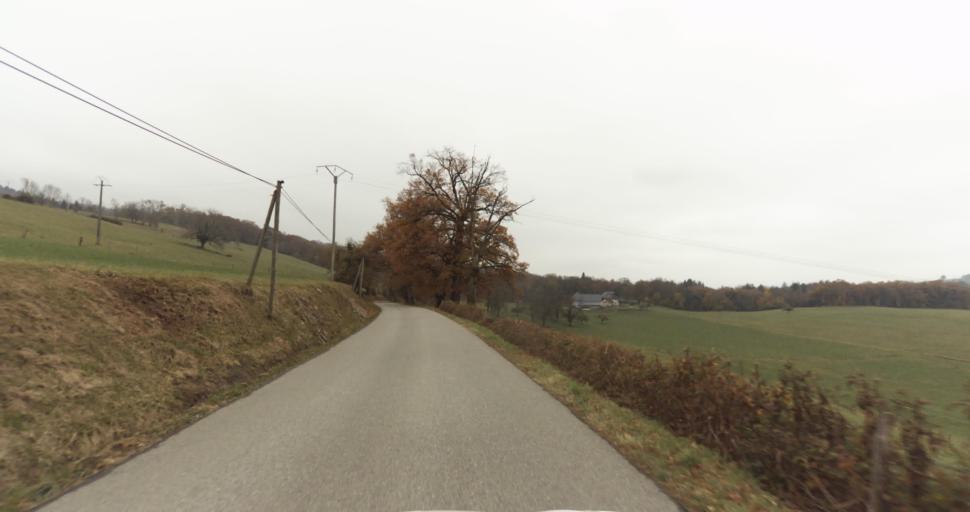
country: FR
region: Rhone-Alpes
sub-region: Departement de la Haute-Savoie
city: Cusy
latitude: 45.7587
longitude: 6.0197
